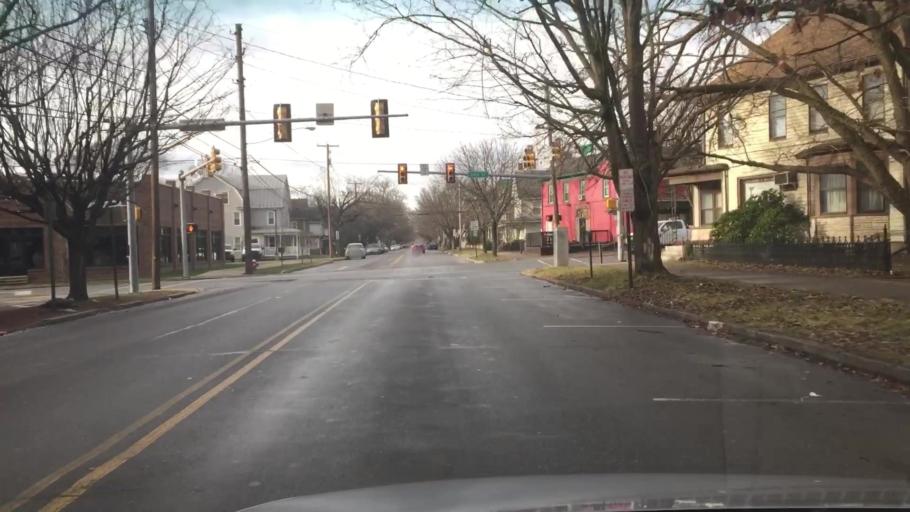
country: US
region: Pennsylvania
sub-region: Columbia County
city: Bloomsburg
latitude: 41.0022
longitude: -76.4489
